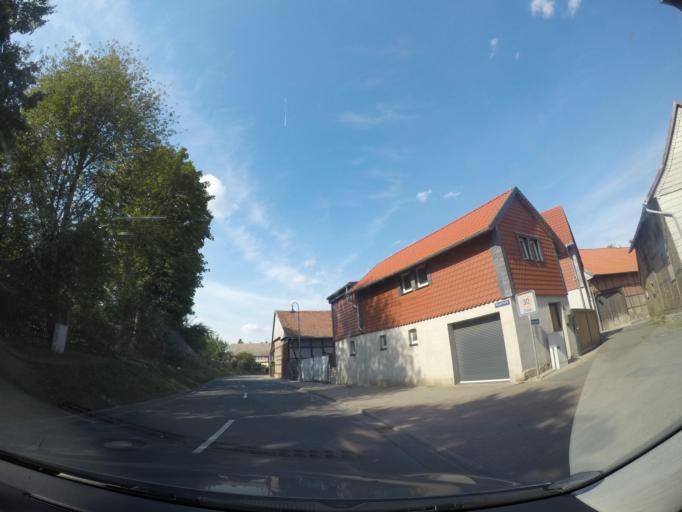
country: DE
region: Saxony-Anhalt
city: Langeln
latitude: 51.9104
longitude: 10.7952
